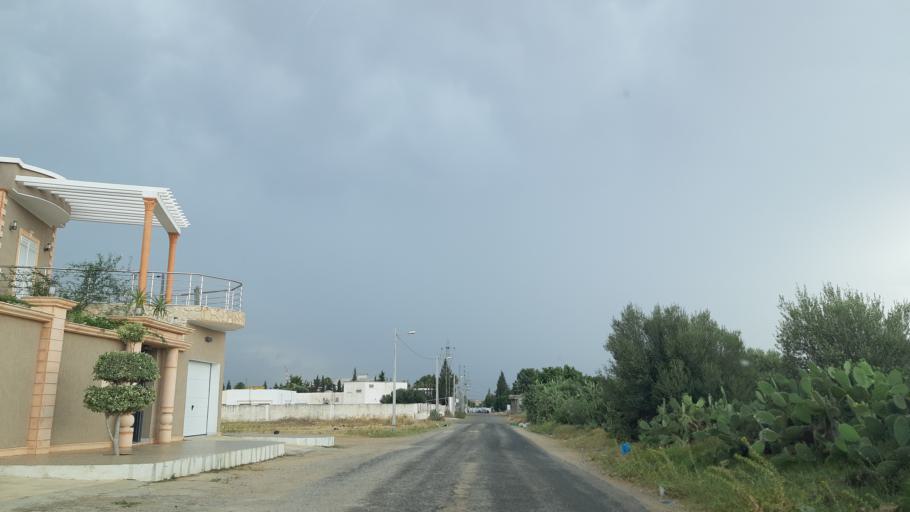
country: TN
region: Al Qayrawan
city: Sbikha
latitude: 36.1237
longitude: 10.0877
